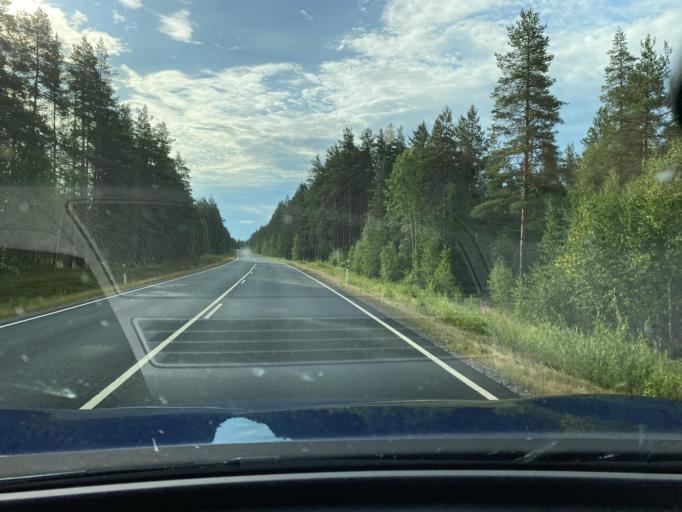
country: FI
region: Central Ostrobothnia
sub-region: Kaustinen
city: Veteli
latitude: 63.4105
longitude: 23.9611
